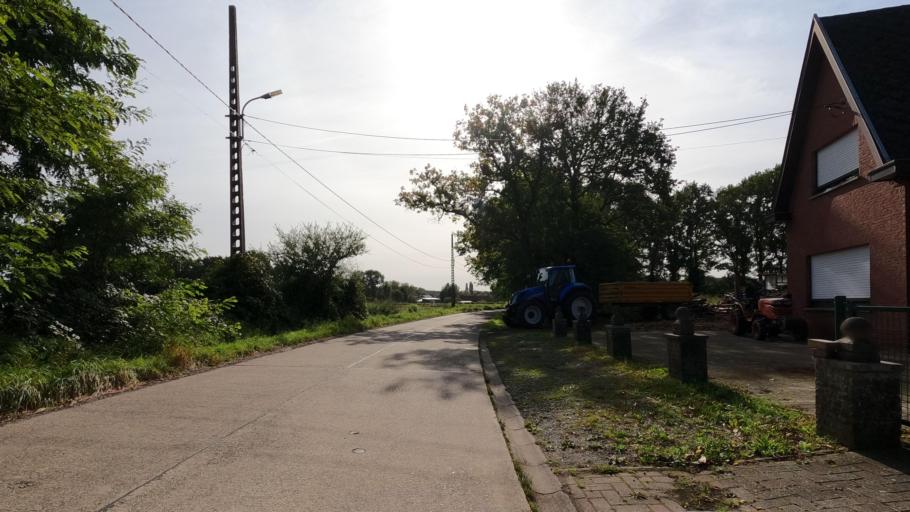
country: BE
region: Flanders
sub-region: Provincie Antwerpen
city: Hulshout
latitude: 51.0708
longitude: 4.8311
